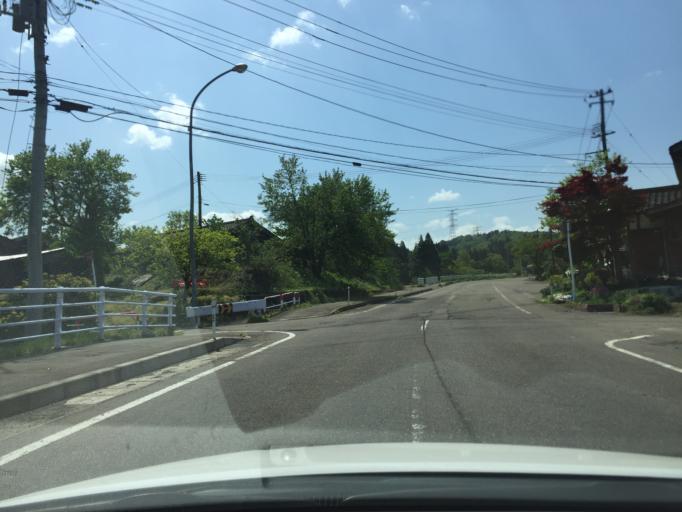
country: JP
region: Niigata
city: Tochio-honcho
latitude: 37.5438
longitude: 139.0929
